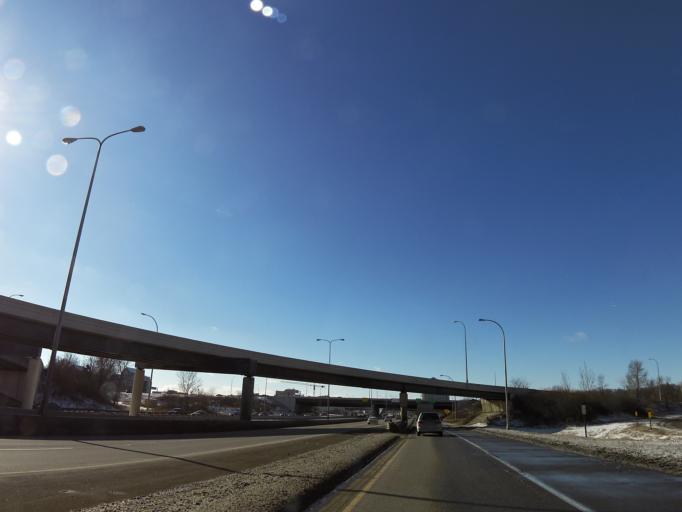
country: US
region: Minnesota
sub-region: Hennepin County
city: Saint Louis Park
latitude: 44.9709
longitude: -93.3368
